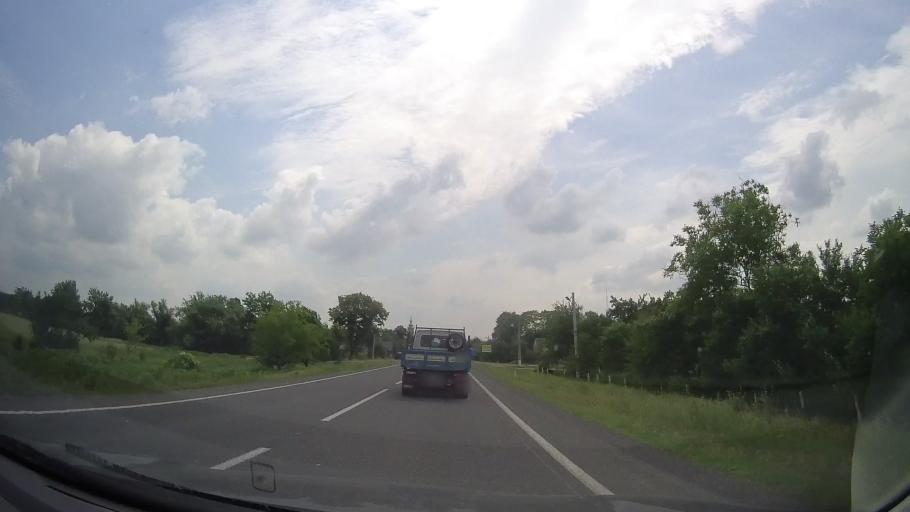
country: RO
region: Timis
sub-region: Comuna Topolovatu Mare
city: Topolovatu Mare
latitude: 45.7893
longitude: 21.5790
